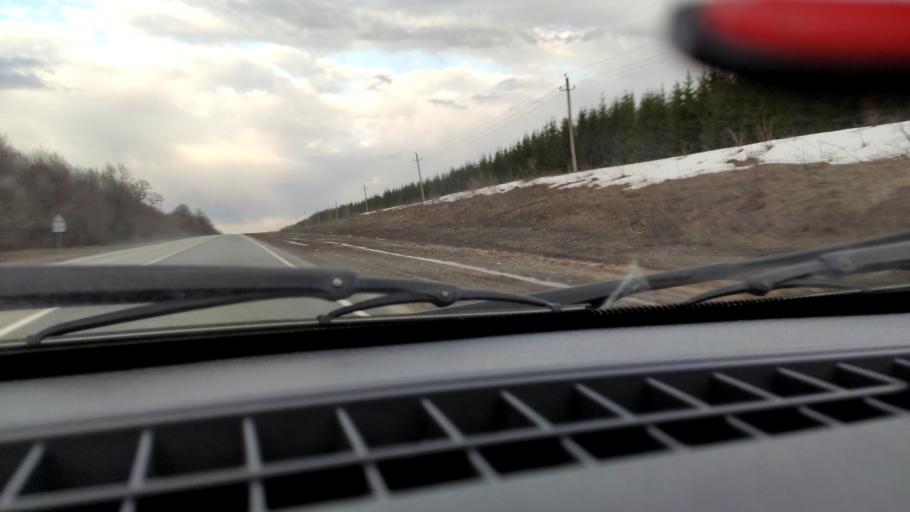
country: RU
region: Bashkortostan
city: Kudeyevskiy
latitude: 54.8036
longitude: 56.6182
